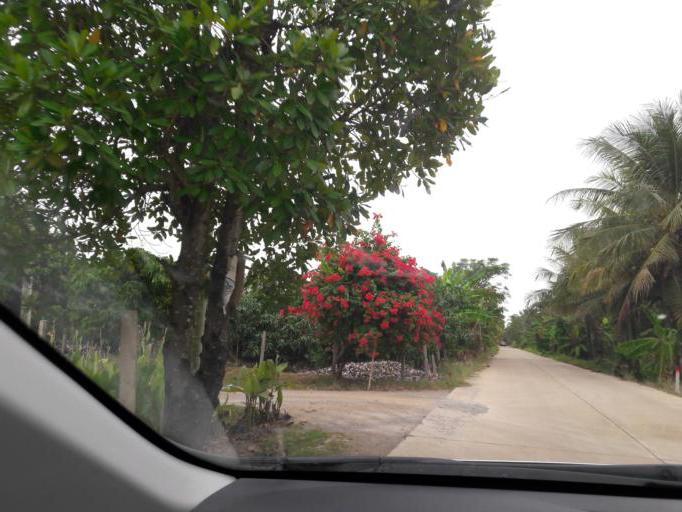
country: TH
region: Samut Sakhon
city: Ban Phaeo
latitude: 13.5964
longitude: 100.0395
